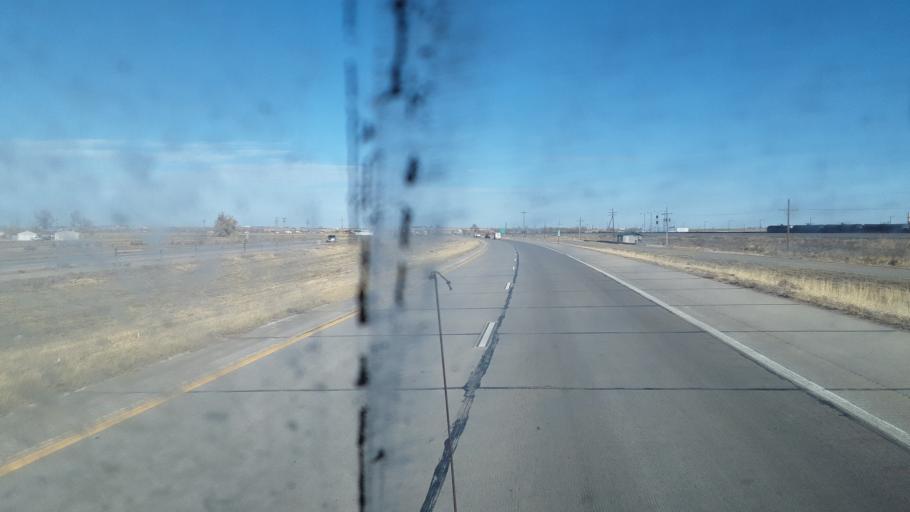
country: US
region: Colorado
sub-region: Weld County
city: Hudson
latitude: 40.0868
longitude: -104.6245
